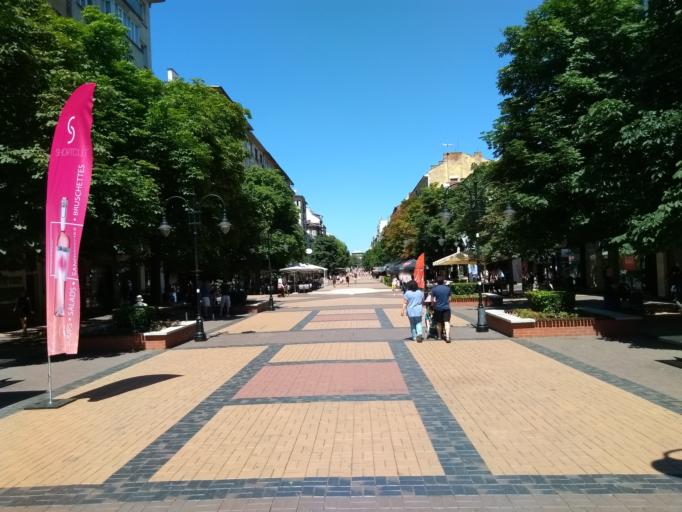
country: BG
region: Sofia-Capital
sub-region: Stolichna Obshtina
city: Sofia
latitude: 42.6905
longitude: 23.3194
